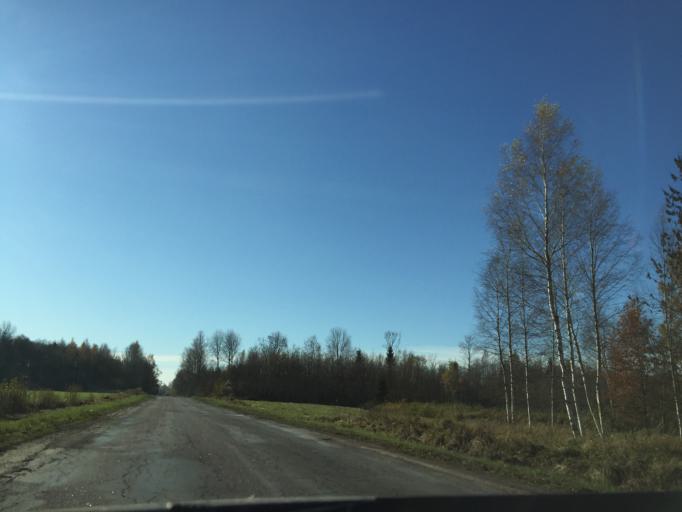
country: LV
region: Skriveri
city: Skriveri
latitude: 56.7220
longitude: 25.1592
